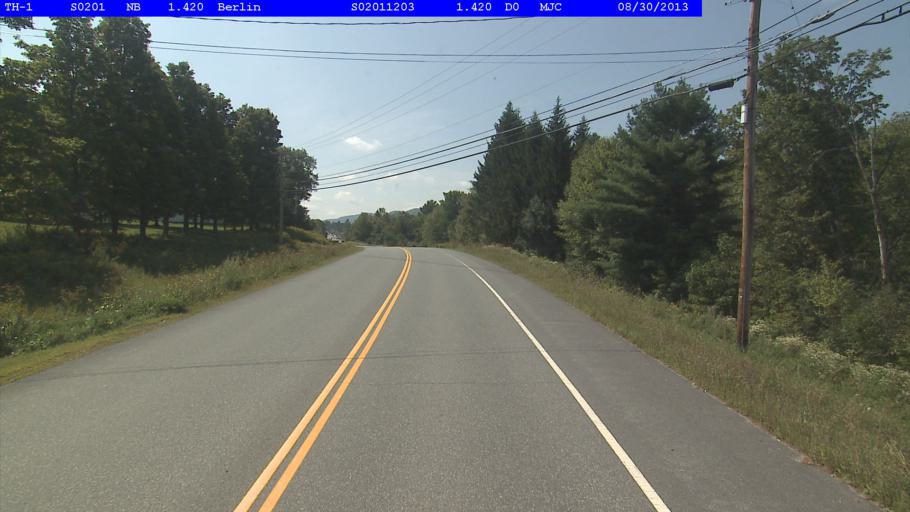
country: US
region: Vermont
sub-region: Washington County
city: Montpelier
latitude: 44.2195
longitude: -72.5712
